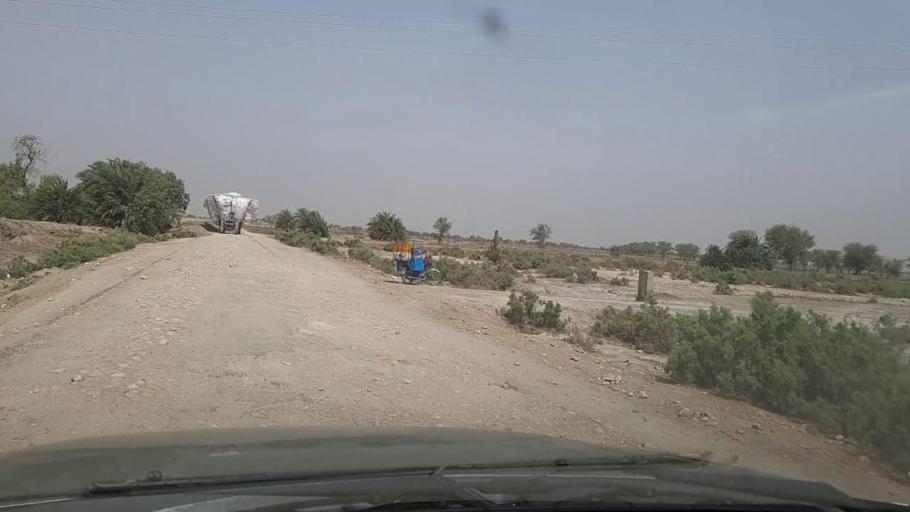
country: PK
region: Sindh
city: Thul
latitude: 28.4105
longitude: 68.6969
